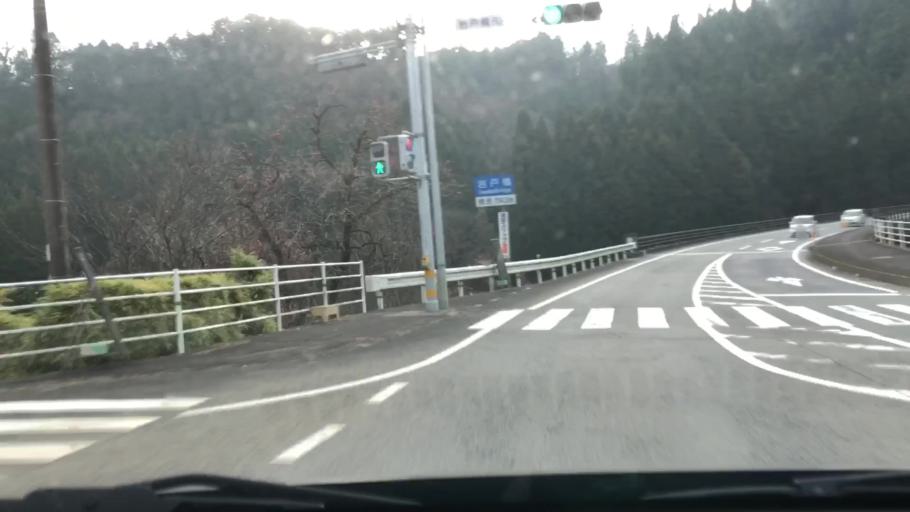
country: JP
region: Oita
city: Takedamachi
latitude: 32.9814
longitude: 131.5486
